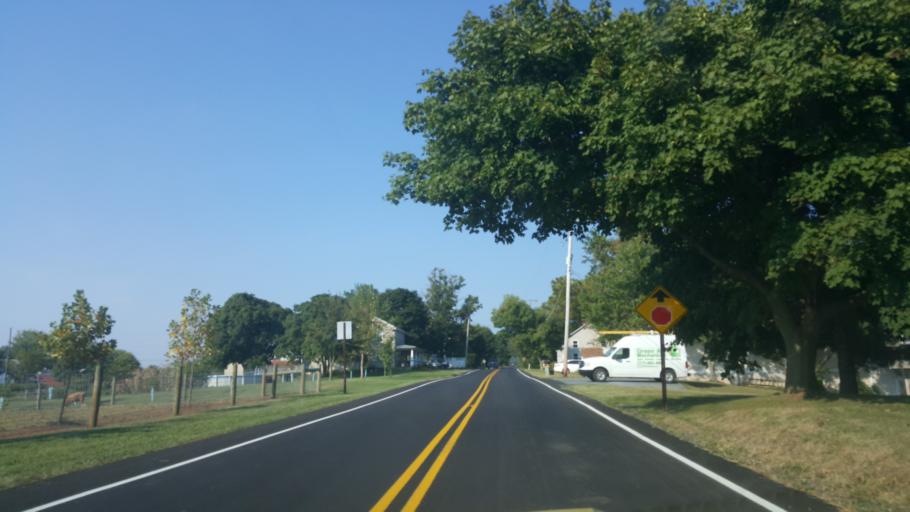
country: US
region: Pennsylvania
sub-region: Lebanon County
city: Campbelltown
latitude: 40.2267
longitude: -76.5525
